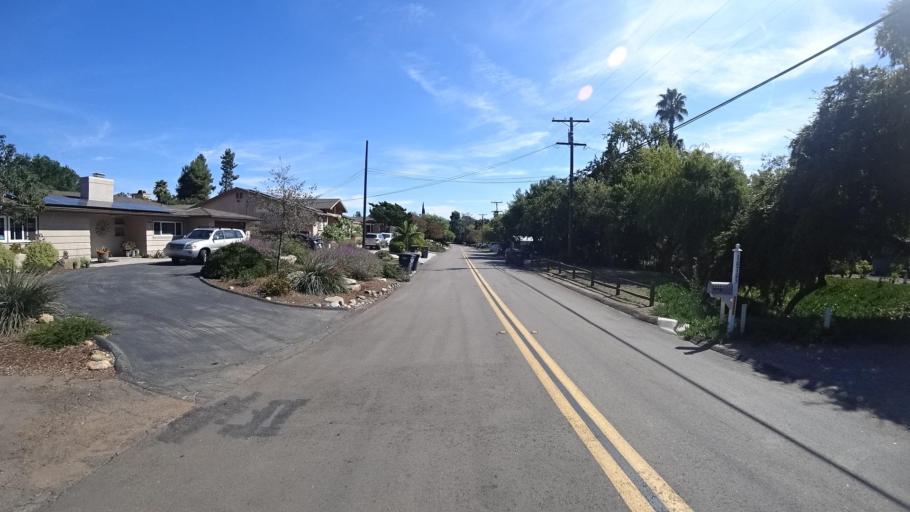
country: US
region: California
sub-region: San Diego County
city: Casa de Oro-Mount Helix
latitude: 32.7509
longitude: -116.9644
